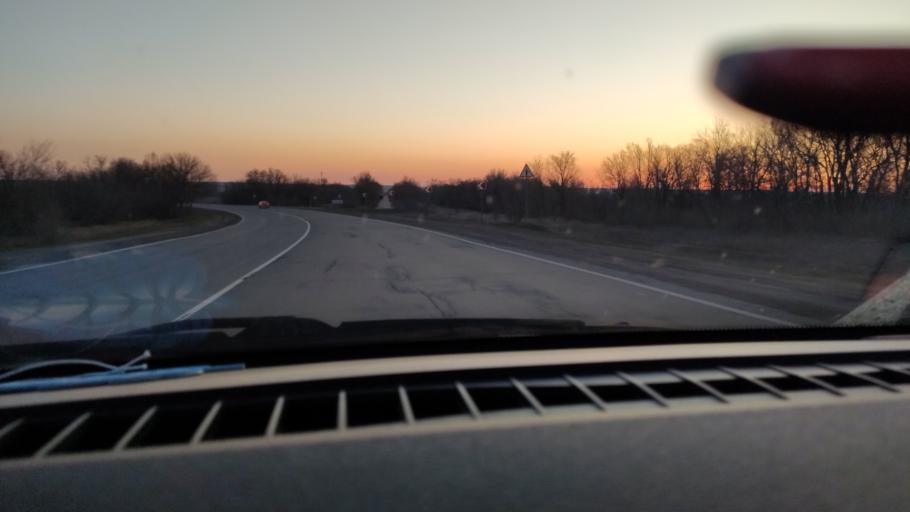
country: RU
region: Saratov
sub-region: Saratovskiy Rayon
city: Saratov
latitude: 51.7147
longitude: 46.0245
